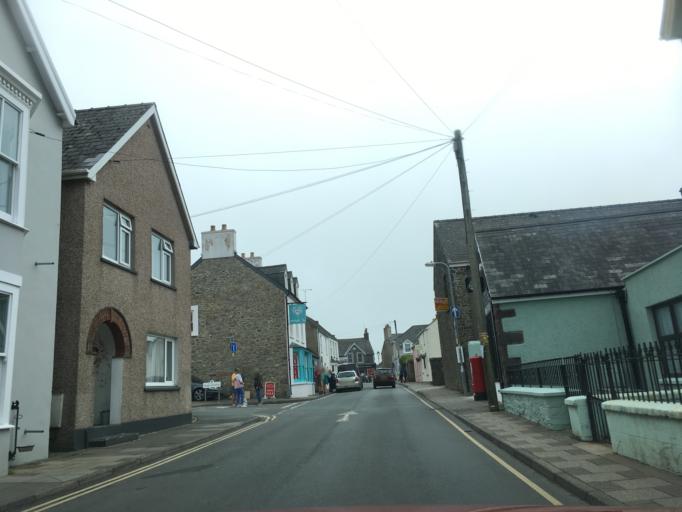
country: GB
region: Wales
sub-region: Pembrokeshire
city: Saint David's
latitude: 51.8817
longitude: -5.2641
